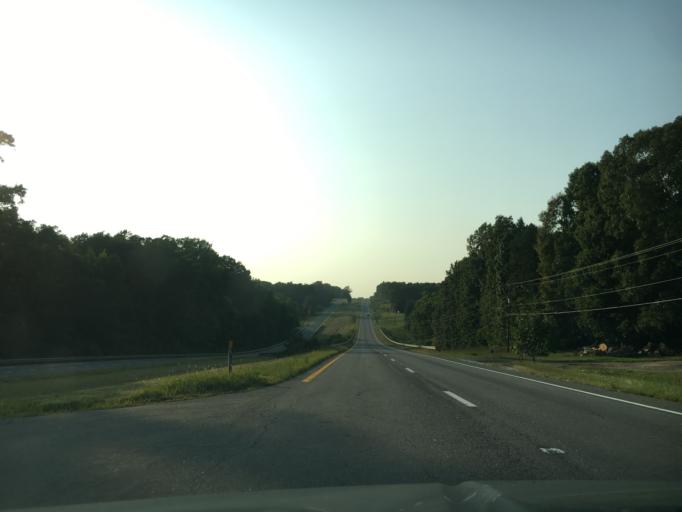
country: US
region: Virginia
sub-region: Appomattox County
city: Appomattox
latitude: 37.3348
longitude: -78.7876
